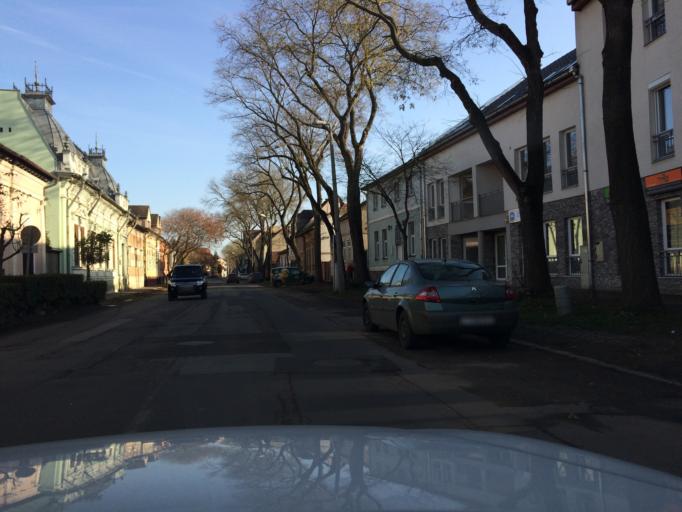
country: HU
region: Szabolcs-Szatmar-Bereg
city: Nyiregyhaza
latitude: 47.9539
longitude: 21.7224
